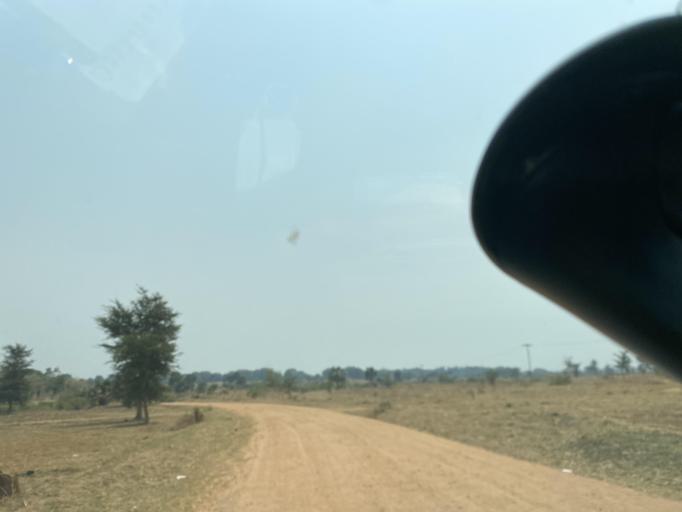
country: ZM
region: Lusaka
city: Kafue
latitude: -15.6308
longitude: 28.0992
